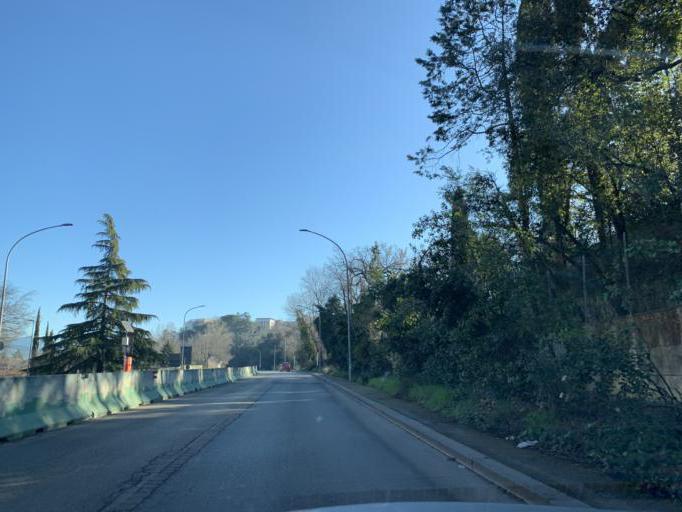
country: IT
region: Umbria
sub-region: Provincia di Terni
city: Terni
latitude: 42.5548
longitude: 12.6498
